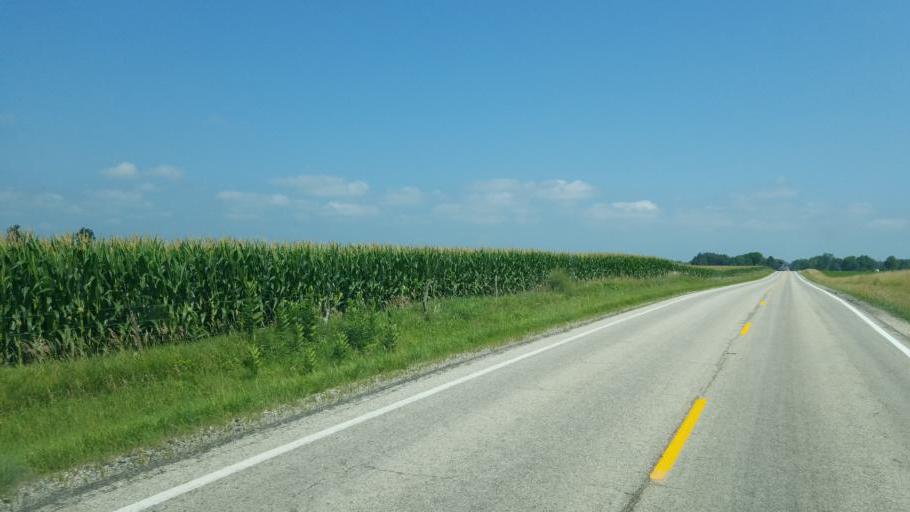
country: US
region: Ohio
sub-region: Crawford County
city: Galion
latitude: 40.8215
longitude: -82.8556
